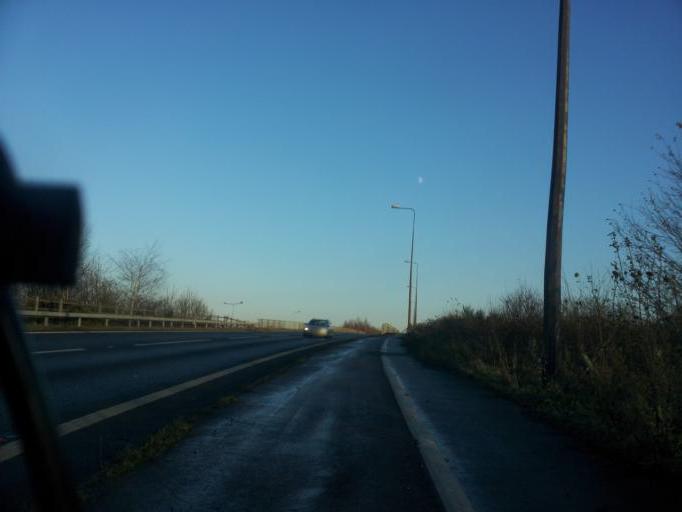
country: GB
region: England
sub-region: Medway
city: Cuxton
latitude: 51.3984
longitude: 0.4483
